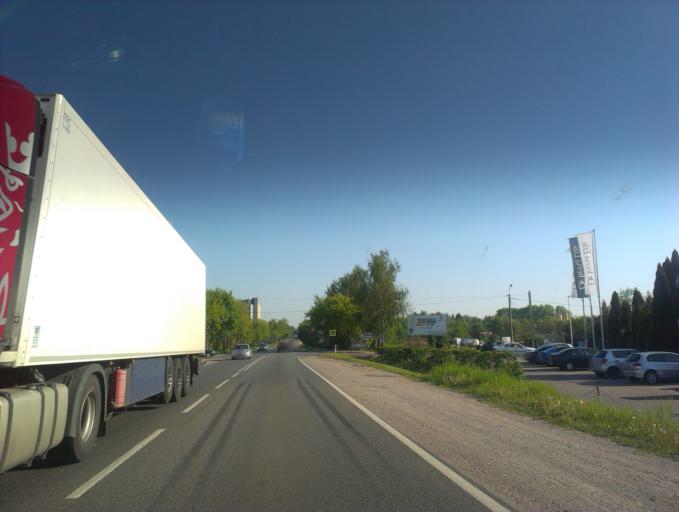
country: PL
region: Masovian Voivodeship
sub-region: Powiat piaseczynski
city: Piaseczno
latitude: 52.0707
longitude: 21.0358
